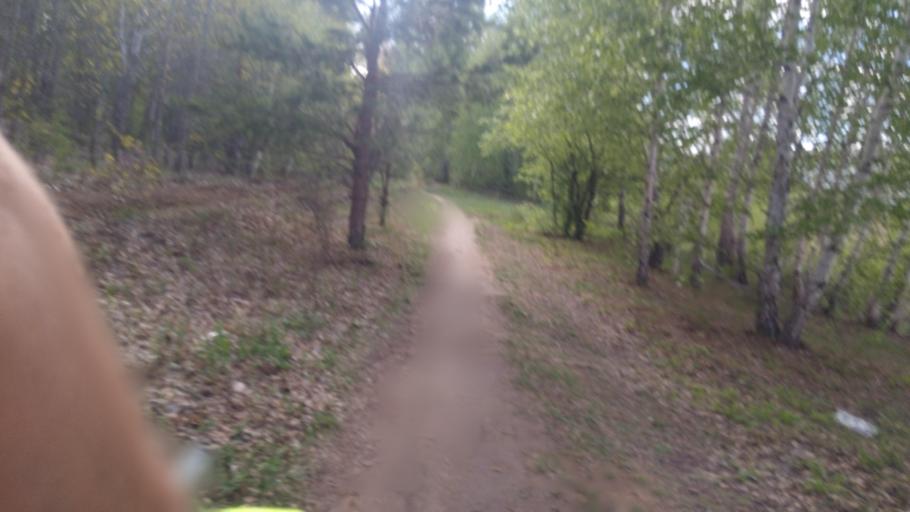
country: RU
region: Chelyabinsk
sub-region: Gorod Chelyabinsk
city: Chelyabinsk
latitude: 55.1678
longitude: 61.3248
